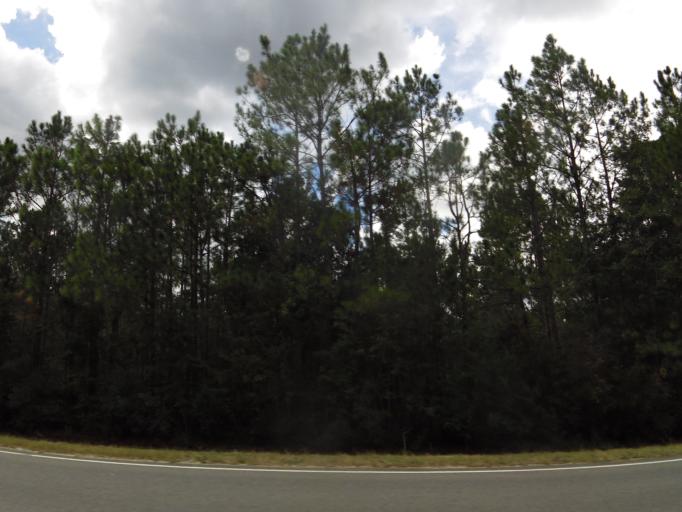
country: US
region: Georgia
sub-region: Brantley County
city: Nahunta
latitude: 31.1858
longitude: -81.9870
